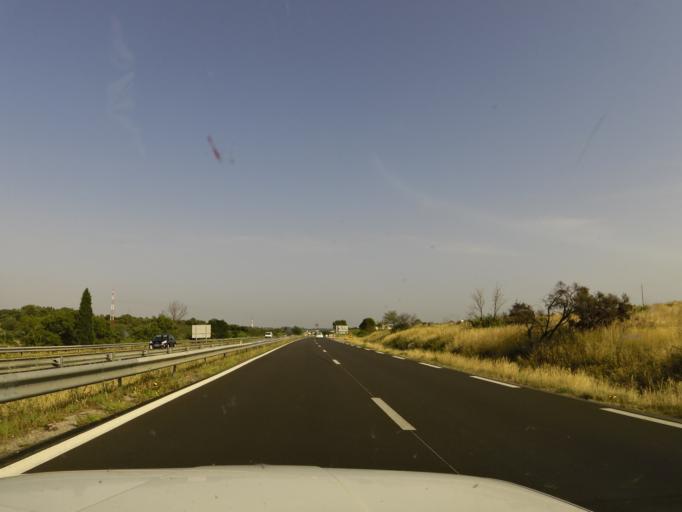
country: FR
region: Languedoc-Roussillon
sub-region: Departement de l'Herault
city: Grabels
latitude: 43.6279
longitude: 3.7825
